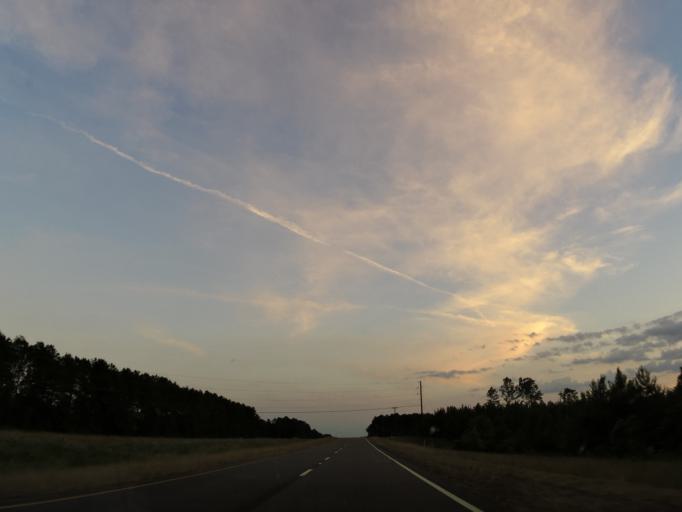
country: US
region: Mississippi
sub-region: Kemper County
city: De Kalb
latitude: 32.7172
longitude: -88.4797
